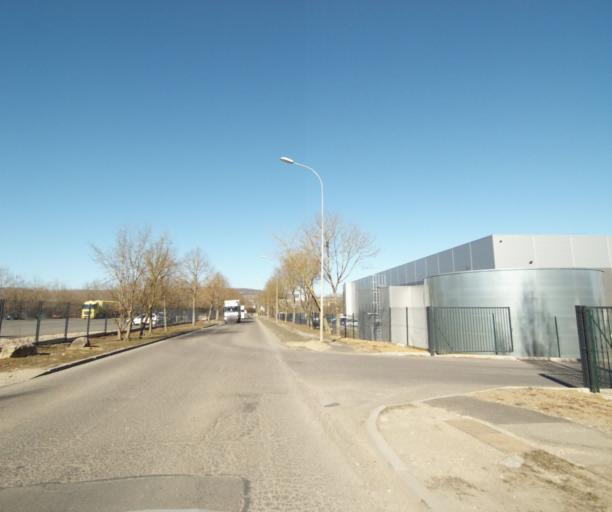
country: FR
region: Lorraine
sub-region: Departement de Meurthe-et-Moselle
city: Fleville-devant-Nancy
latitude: 48.6085
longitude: 6.1935
